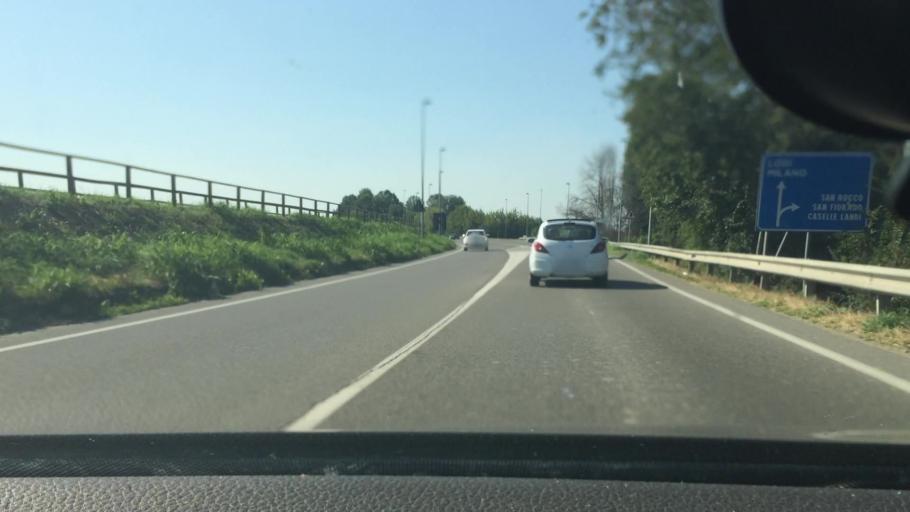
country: IT
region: Lombardy
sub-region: Provincia di Lodi
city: San Rocco al Porto
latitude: 45.0756
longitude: 9.7054
